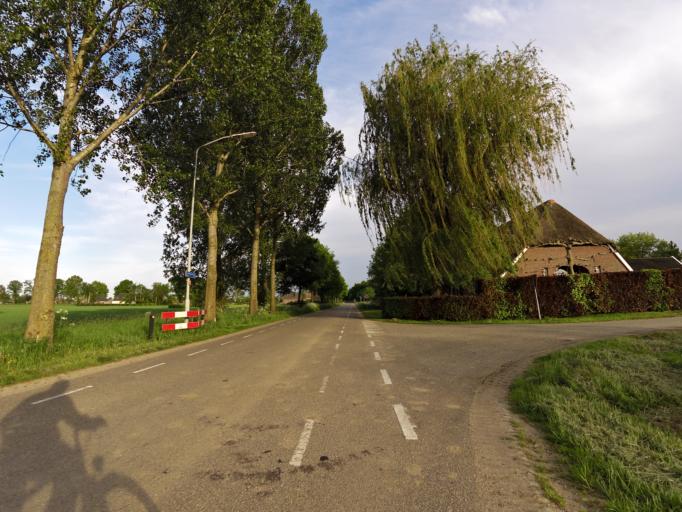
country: NL
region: Gelderland
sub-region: Oude IJsselstreek
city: Gendringen
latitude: 51.8721
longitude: 6.3482
